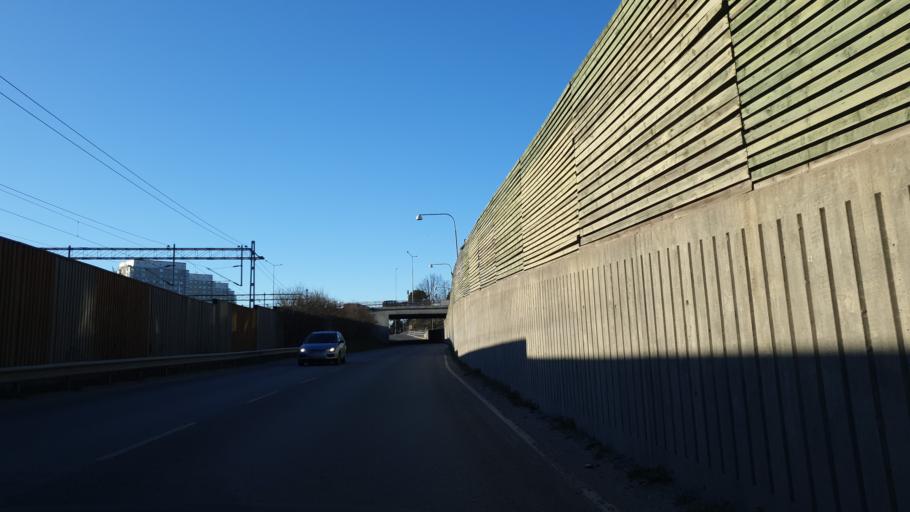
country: SE
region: Stockholm
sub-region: Solna Kommun
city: Solna
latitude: 59.3757
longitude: 18.0047
